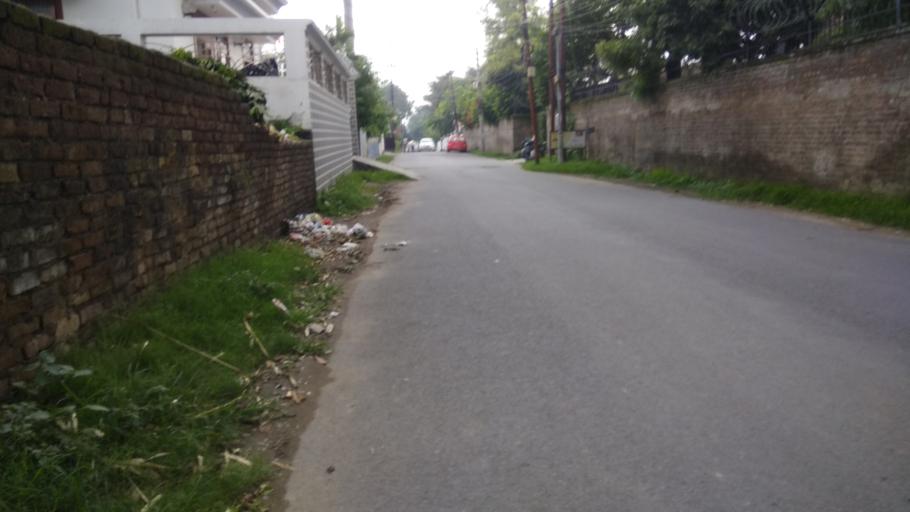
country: IN
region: Uttarakhand
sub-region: Dehradun
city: Dehradun
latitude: 30.3150
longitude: 78.0576
